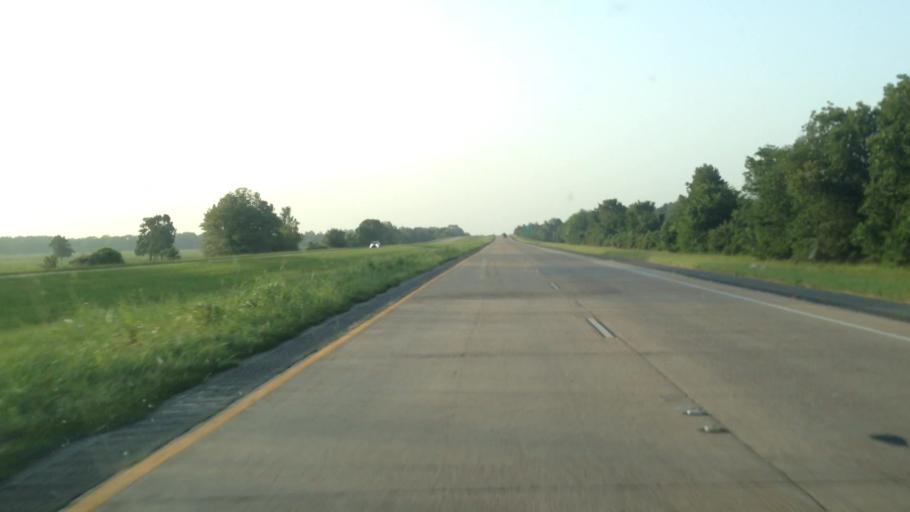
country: US
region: Louisiana
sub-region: Natchitoches Parish
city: Vienna Bend
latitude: 31.6303
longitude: -93.0697
